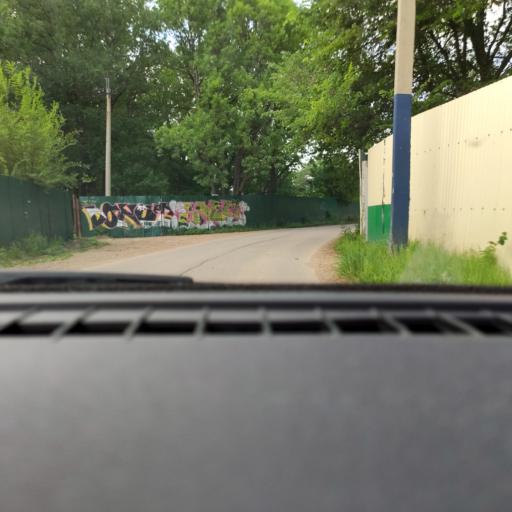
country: RU
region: Samara
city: Volzhskiy
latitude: 53.4213
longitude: 50.1162
